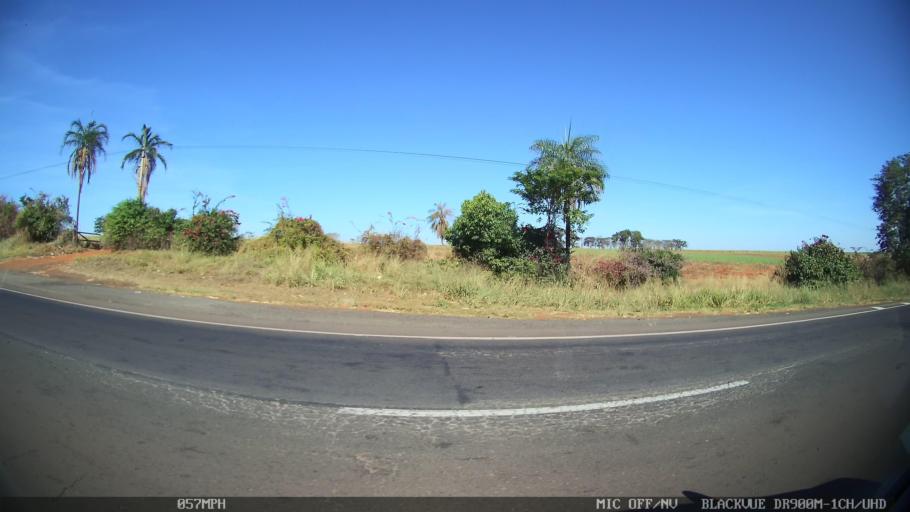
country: BR
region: Sao Paulo
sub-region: Olimpia
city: Olimpia
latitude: -20.6724
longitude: -48.8785
